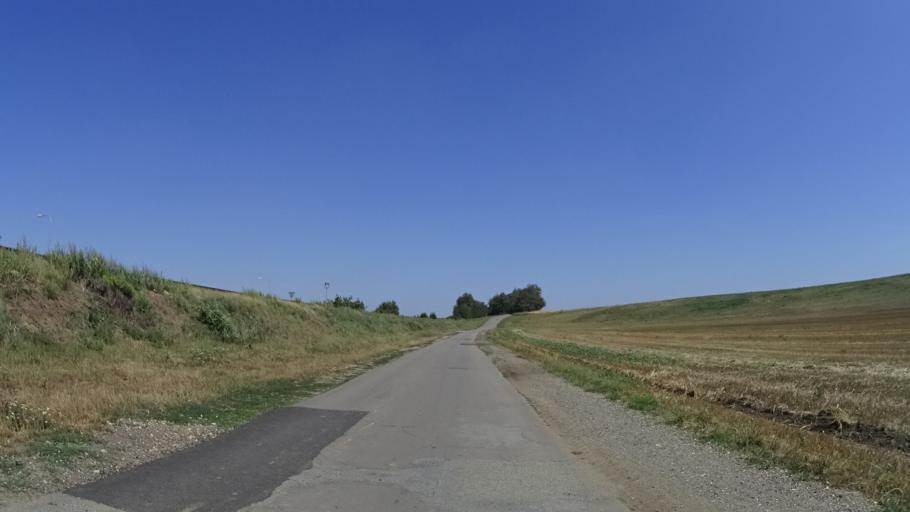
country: CZ
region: South Moravian
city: Petrov
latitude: 48.8845
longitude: 17.2873
